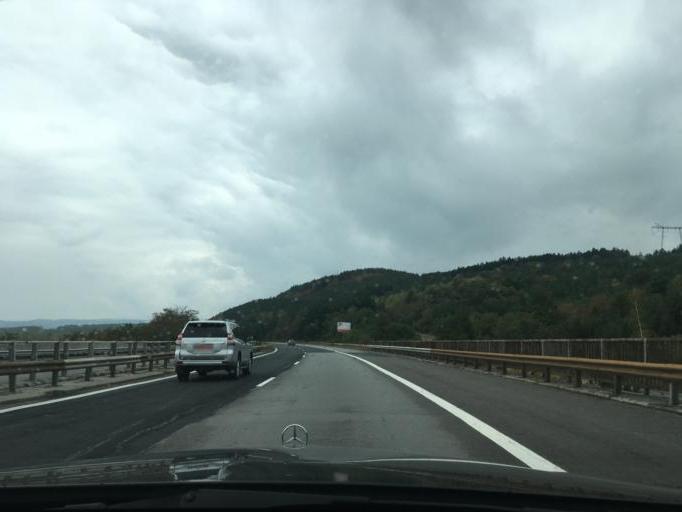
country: BG
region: Sofiya
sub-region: Obshtina Elin Pelin
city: Elin Pelin
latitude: 42.5943
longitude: 23.5919
